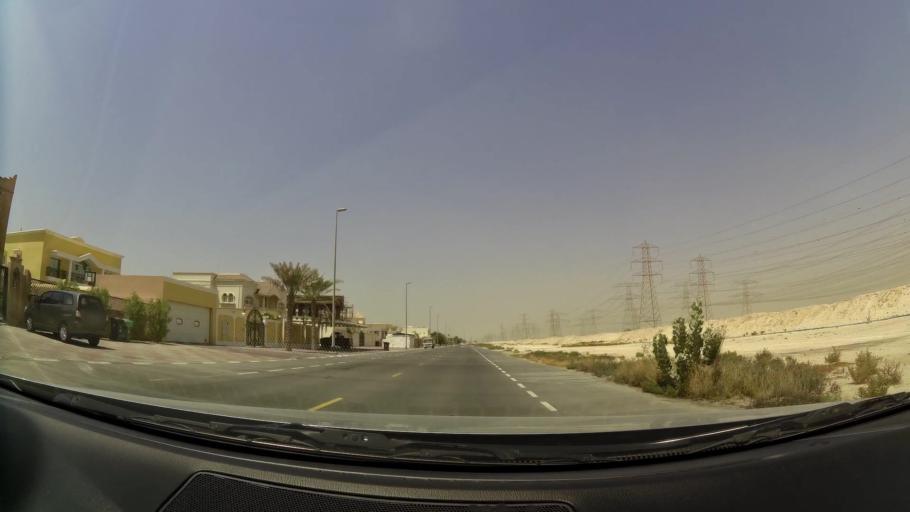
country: AE
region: Dubai
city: Dubai
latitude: 25.0928
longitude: 55.2193
